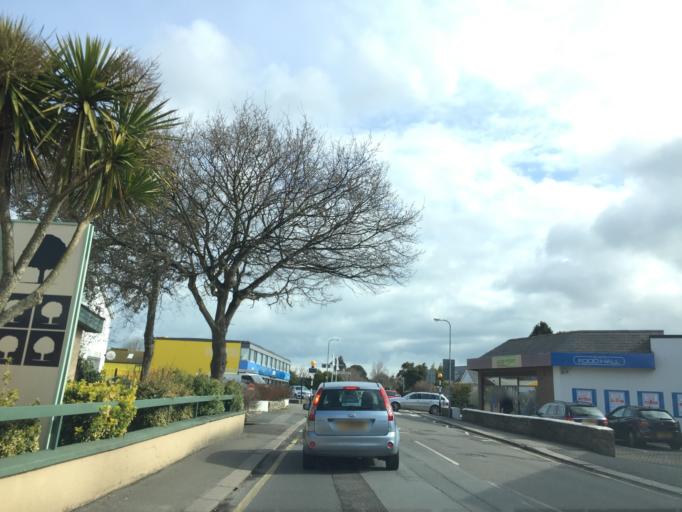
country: JE
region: St Helier
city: Saint Helier
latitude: 49.1983
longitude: -2.0811
